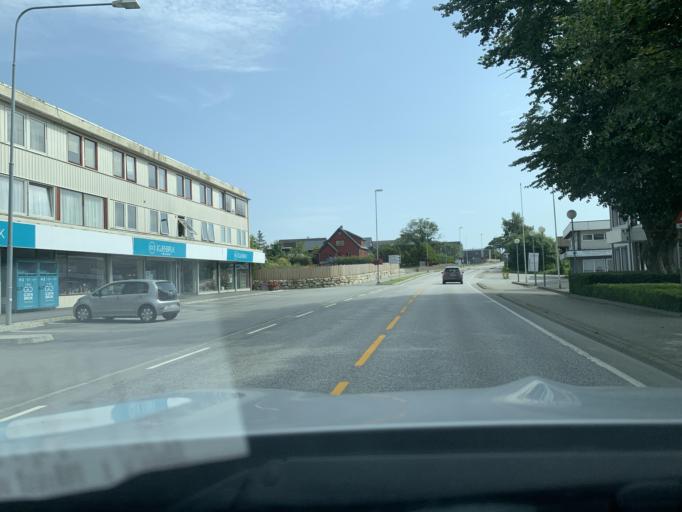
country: NO
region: Rogaland
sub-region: Klepp
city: Kleppe
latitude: 58.7731
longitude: 5.6296
